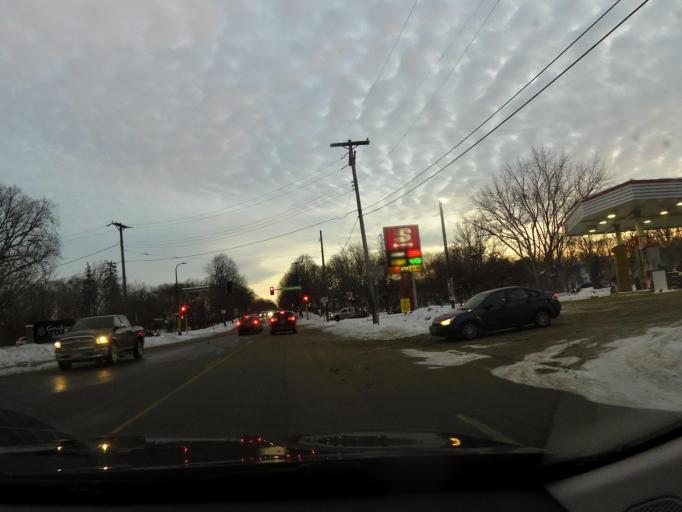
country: US
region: Minnesota
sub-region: Hennepin County
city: Richfield
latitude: 44.9168
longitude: -93.2473
